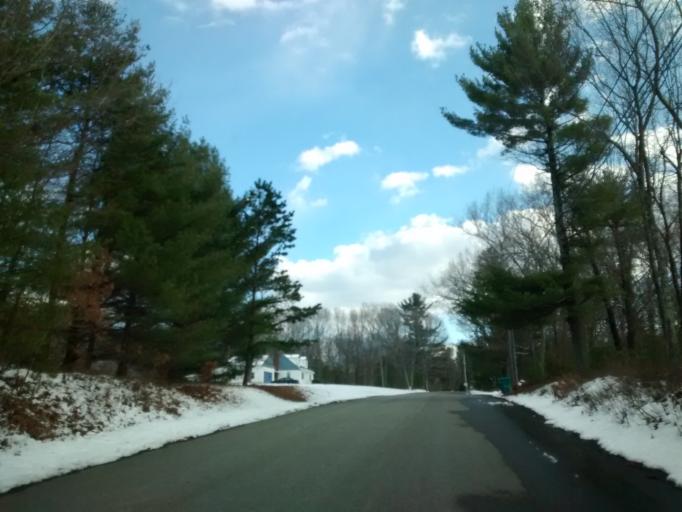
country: US
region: Massachusetts
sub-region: Worcester County
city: Uxbridge
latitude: 42.0313
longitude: -71.6570
